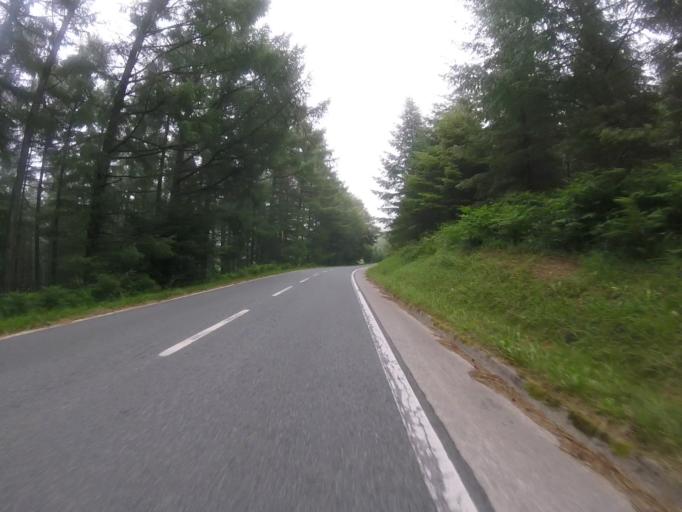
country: ES
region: Navarre
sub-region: Provincia de Navarra
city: Ezkurra
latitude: 43.0831
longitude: -1.8595
